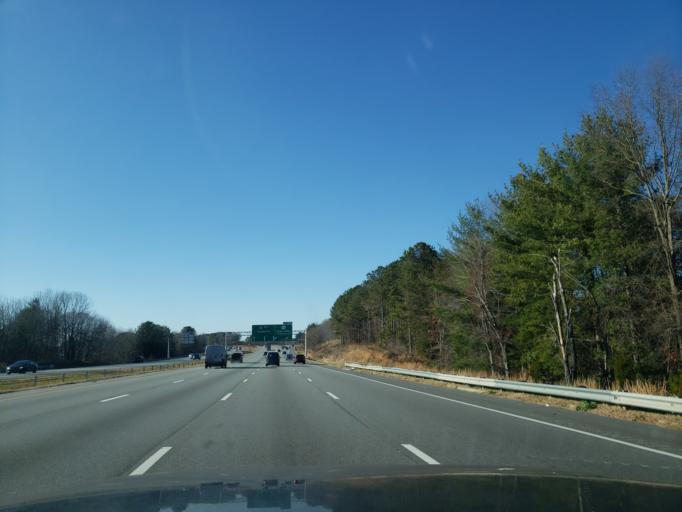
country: US
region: North Carolina
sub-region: Forsyth County
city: Winston-Salem
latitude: 36.0684
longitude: -80.3141
